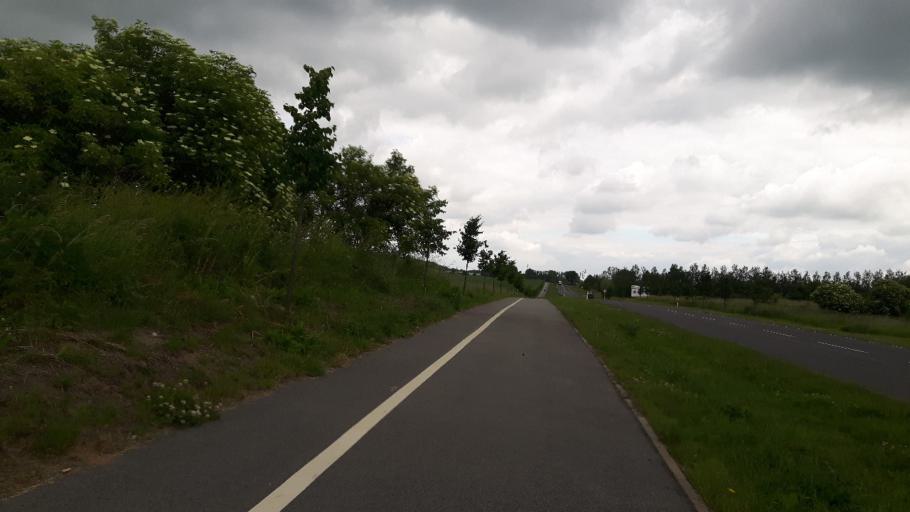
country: PL
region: West Pomeranian Voivodeship
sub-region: Powiat policki
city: Kolbaskowo
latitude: 53.3287
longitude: 14.4259
